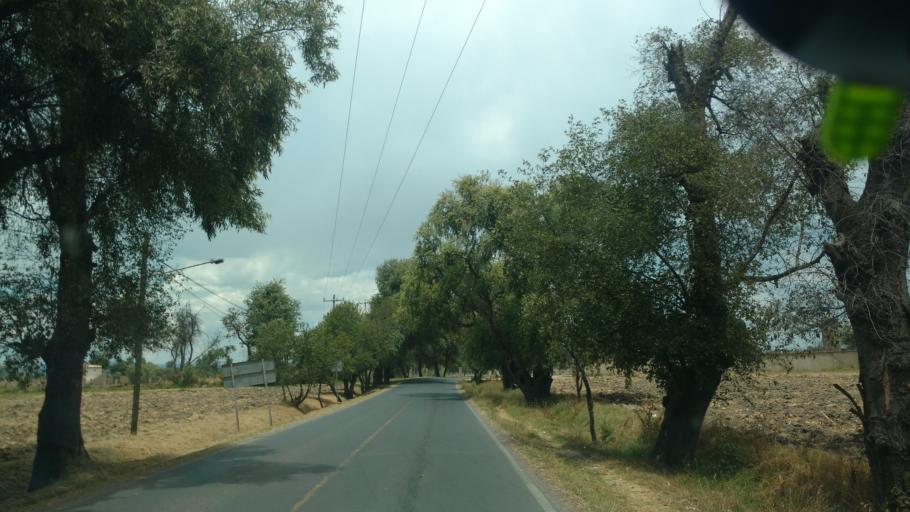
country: MX
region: Puebla
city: San Miguel Xoxtla
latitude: 19.1865
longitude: -98.2949
